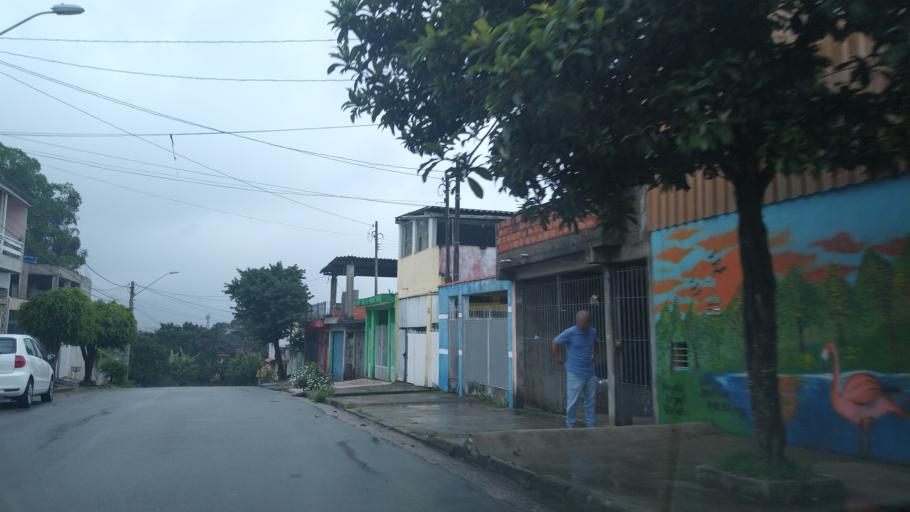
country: BR
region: Sao Paulo
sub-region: Aruja
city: Aruja
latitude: -23.4080
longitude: -46.4024
